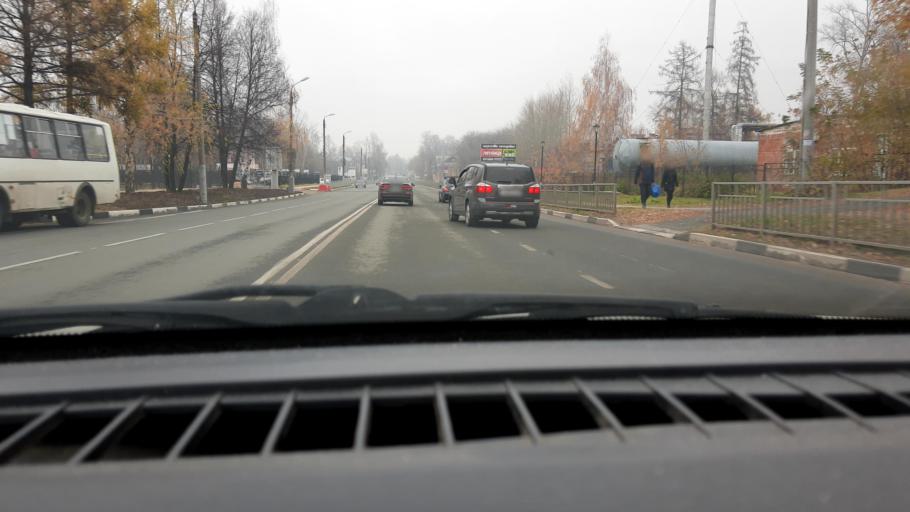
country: RU
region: Nizjnij Novgorod
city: Kstovo
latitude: 56.1525
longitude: 44.1901
